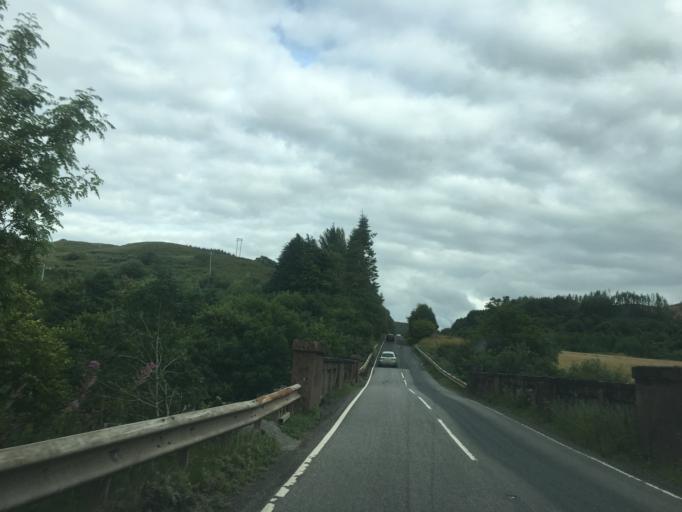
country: GB
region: Scotland
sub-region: Argyll and Bute
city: Oban
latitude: 56.3205
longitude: -5.4944
